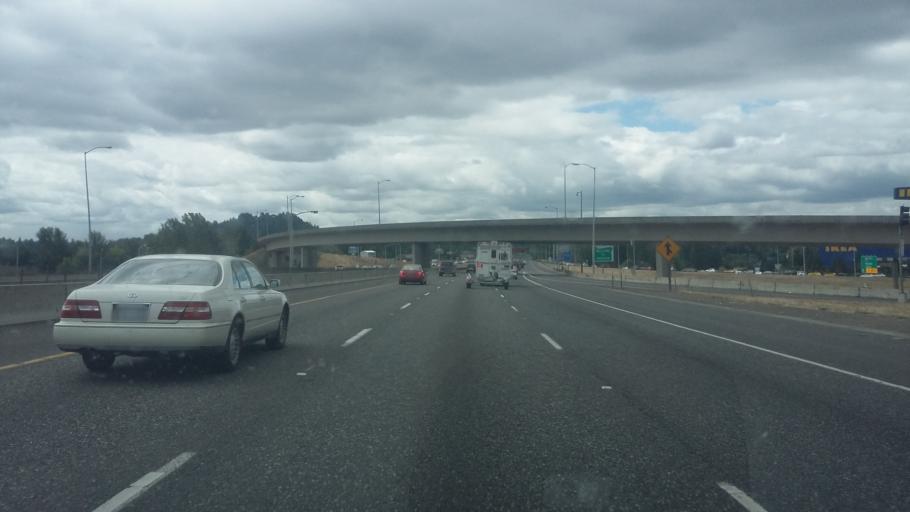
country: US
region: Washington
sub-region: Clark County
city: Mill Plain
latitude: 45.5724
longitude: -122.5483
